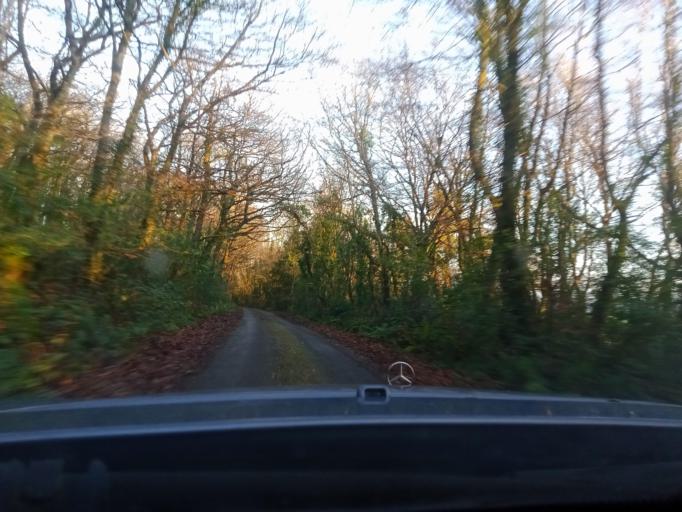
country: IE
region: Leinster
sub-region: Kilkenny
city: Graiguenamanagh
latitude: 52.4690
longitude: -6.9492
